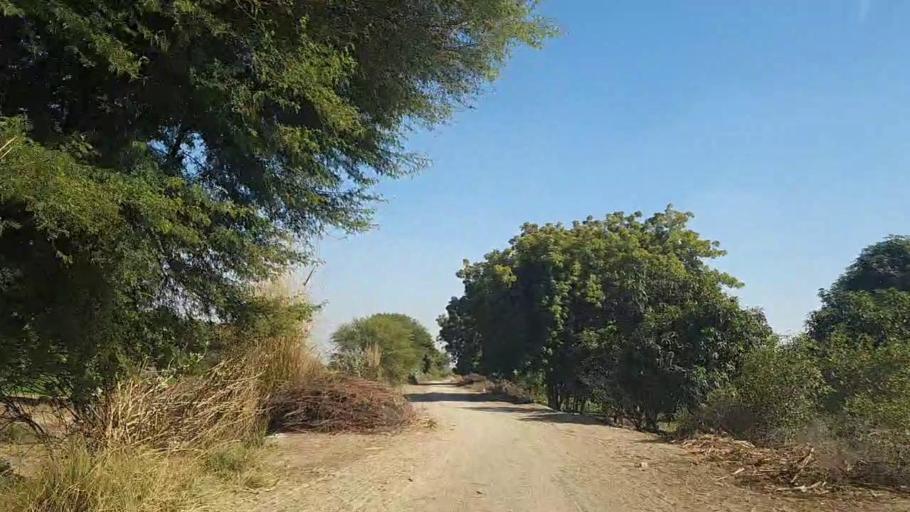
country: PK
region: Sindh
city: Sakrand
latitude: 26.2435
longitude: 68.2026
